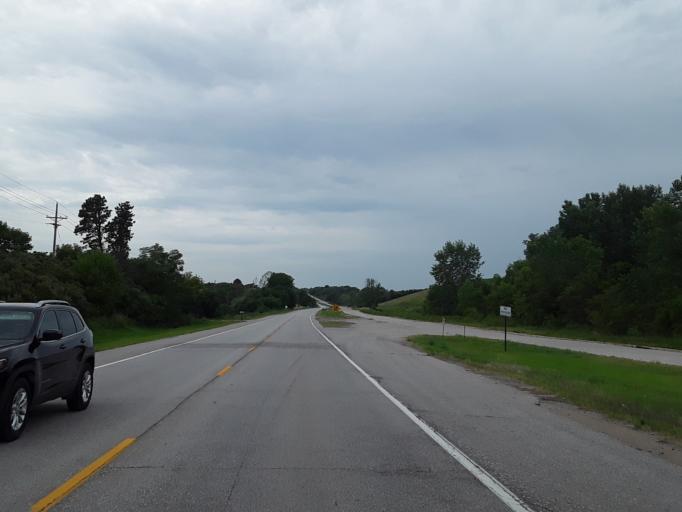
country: US
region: Nebraska
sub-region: Douglas County
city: Bennington
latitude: 41.3647
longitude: -96.0448
